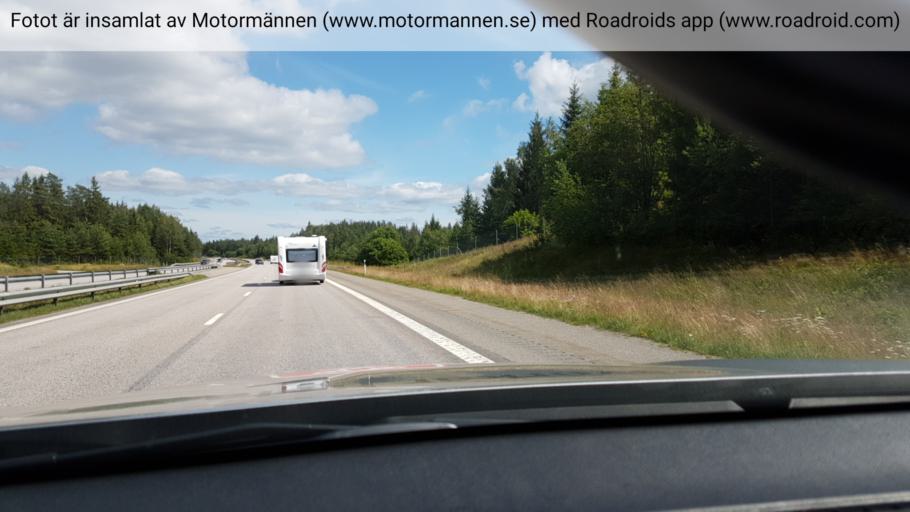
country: SE
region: Vaestra Goetaland
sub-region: Bollebygds Kommun
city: Bollebygd
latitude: 57.6700
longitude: 12.6372
